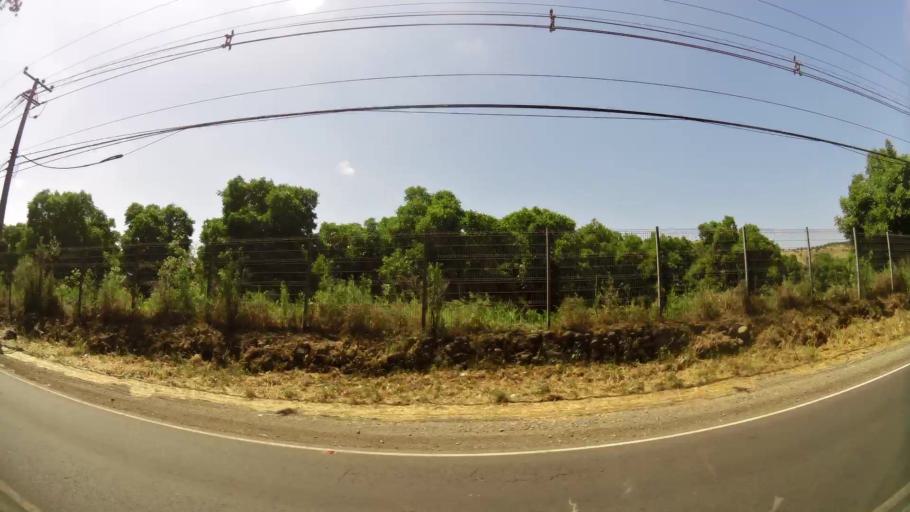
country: CL
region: Santiago Metropolitan
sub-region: Provincia de Maipo
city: San Bernardo
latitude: -33.5679
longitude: -70.7645
